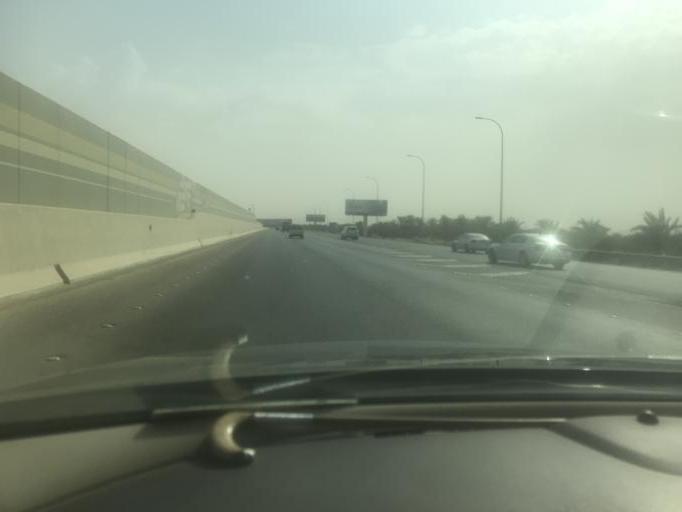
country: SA
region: Ar Riyad
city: Riyadh
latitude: 24.9067
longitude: 46.7139
